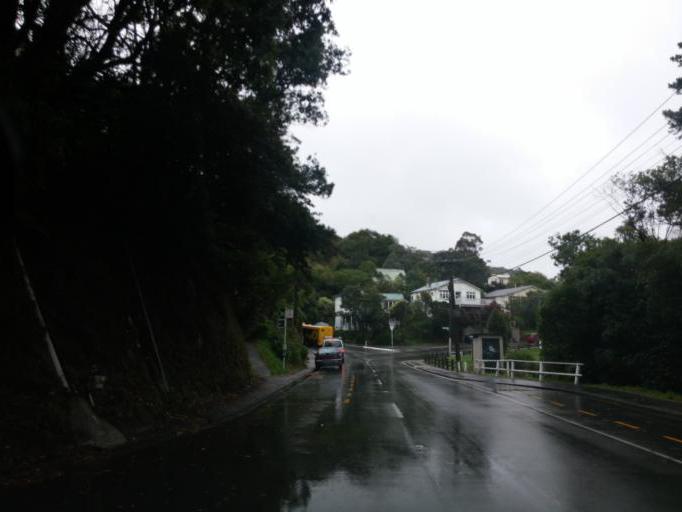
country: NZ
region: Wellington
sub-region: Wellington City
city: Kelburn
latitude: -41.2642
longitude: 174.7642
